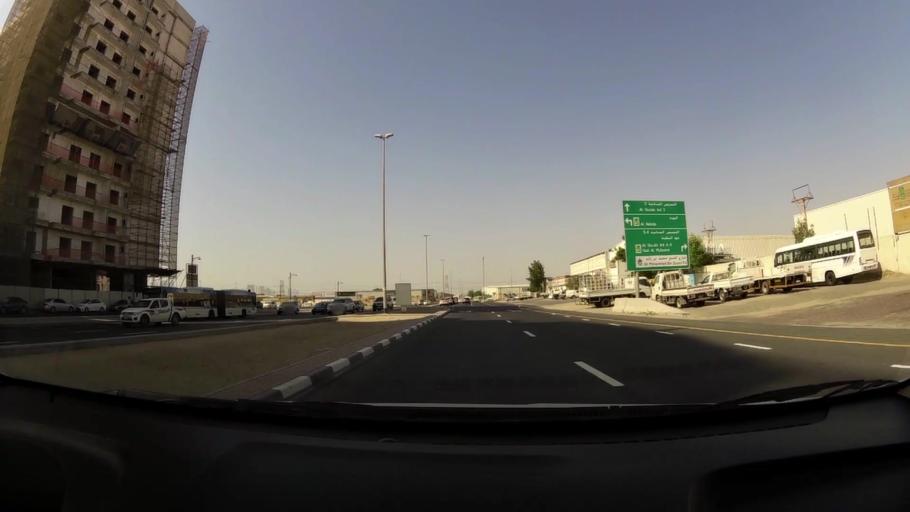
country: AE
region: Ash Shariqah
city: Sharjah
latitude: 25.2942
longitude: 55.3874
